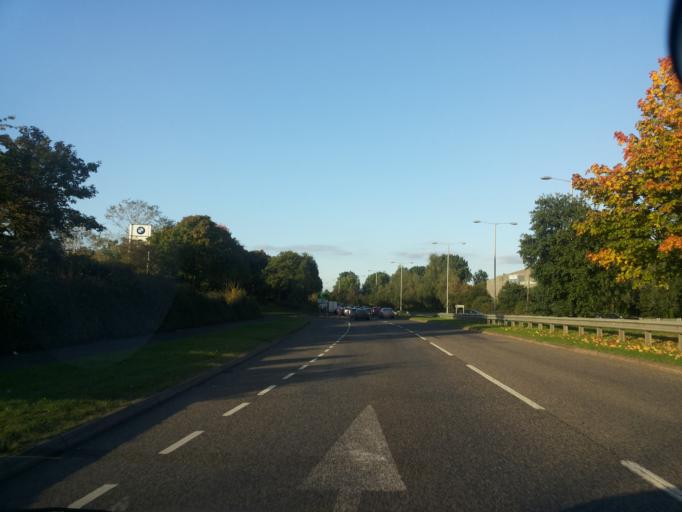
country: GB
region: England
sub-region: Milton Keynes
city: Broughton
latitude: 52.0501
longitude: -0.7051
